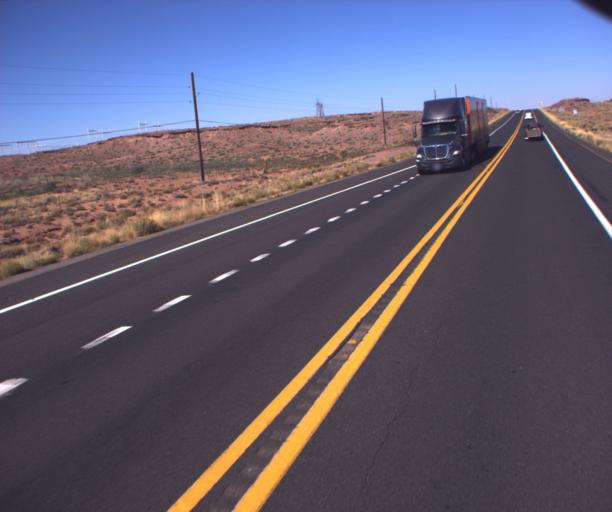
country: US
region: Arizona
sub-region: Coconino County
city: Tuba City
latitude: 35.8247
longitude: -111.4397
